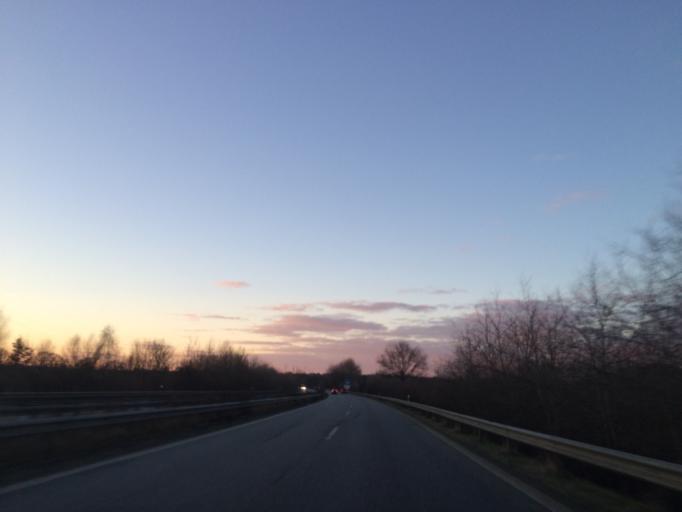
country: DE
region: Schleswig-Holstein
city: Neustadt in Holstein
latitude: 54.1183
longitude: 10.7882
